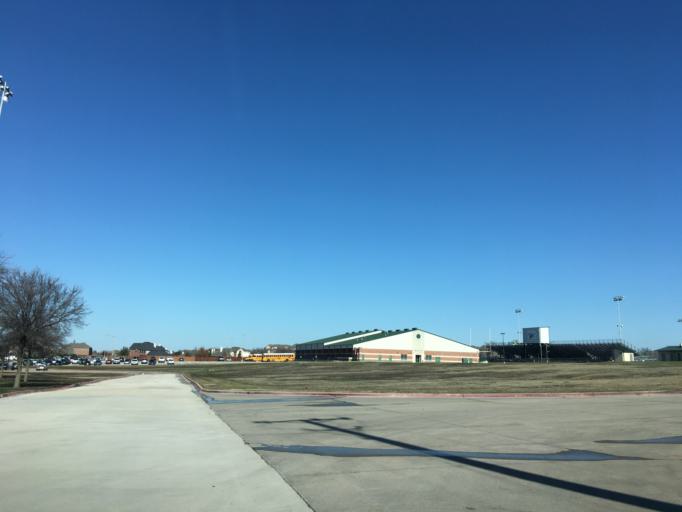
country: US
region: Texas
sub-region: Collin County
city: Prosper
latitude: 33.2410
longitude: -96.7982
